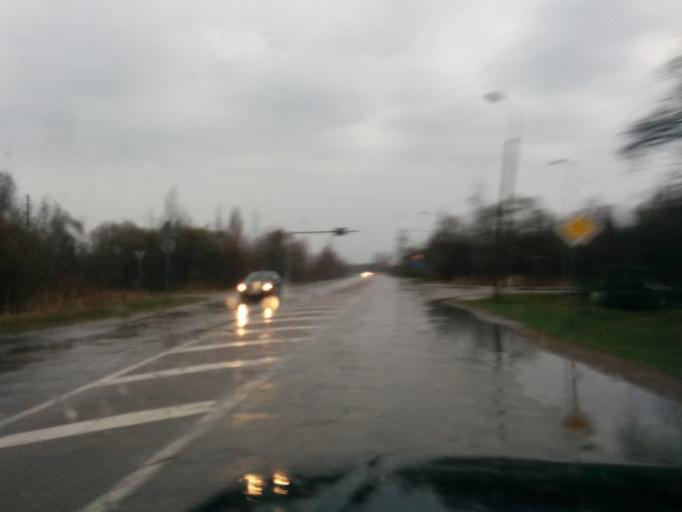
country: LV
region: Ozolnieku
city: Ozolnieki
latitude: 56.6585
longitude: 23.7896
